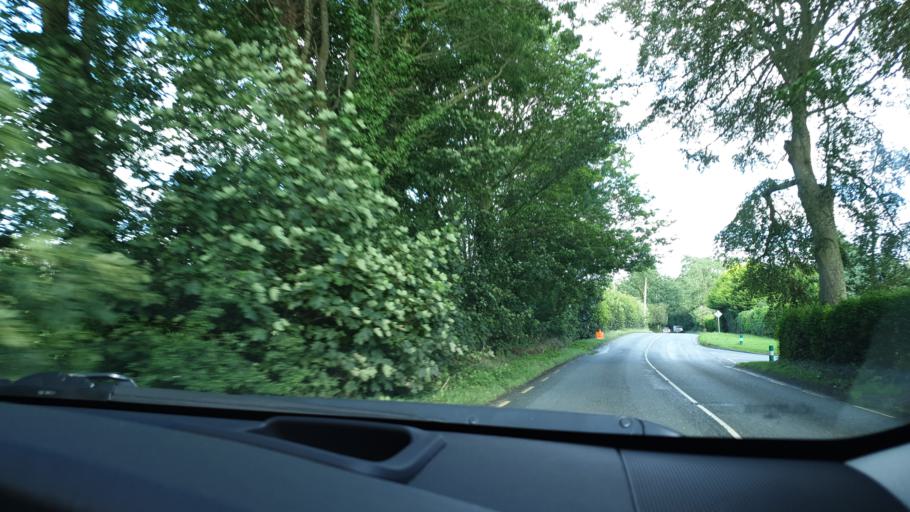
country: IE
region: Leinster
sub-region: An Mhi
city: Ashbourne
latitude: 53.4955
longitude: -6.3943
